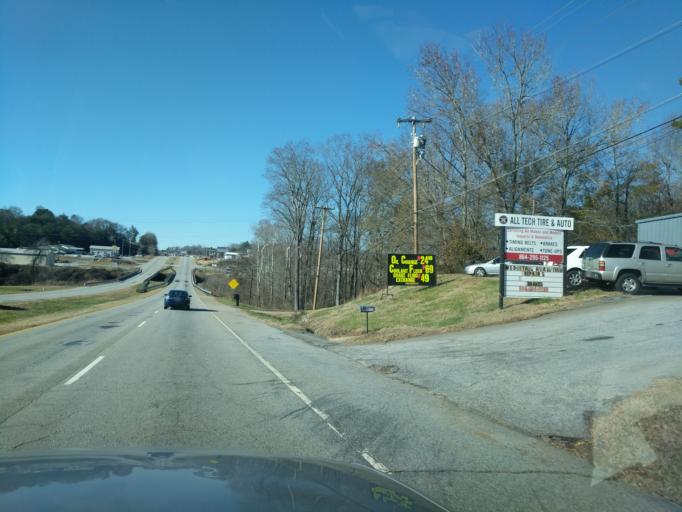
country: US
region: South Carolina
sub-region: Anderson County
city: Powdersville
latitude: 34.8315
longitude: -82.4928
